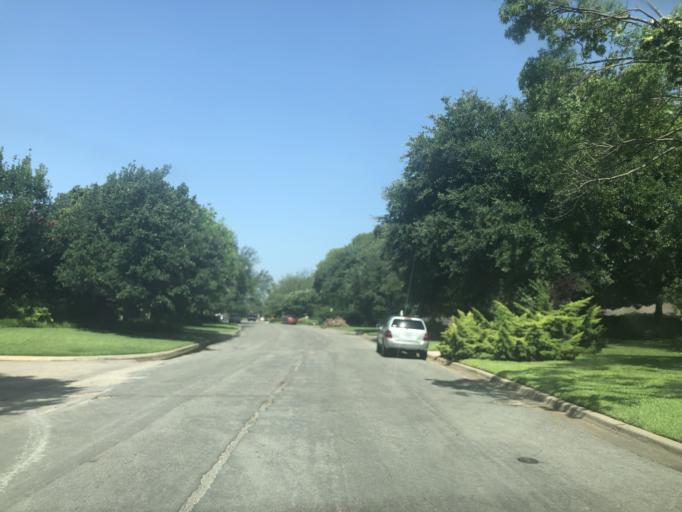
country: US
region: Texas
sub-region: Dallas County
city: University Park
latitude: 32.8867
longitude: -96.8150
